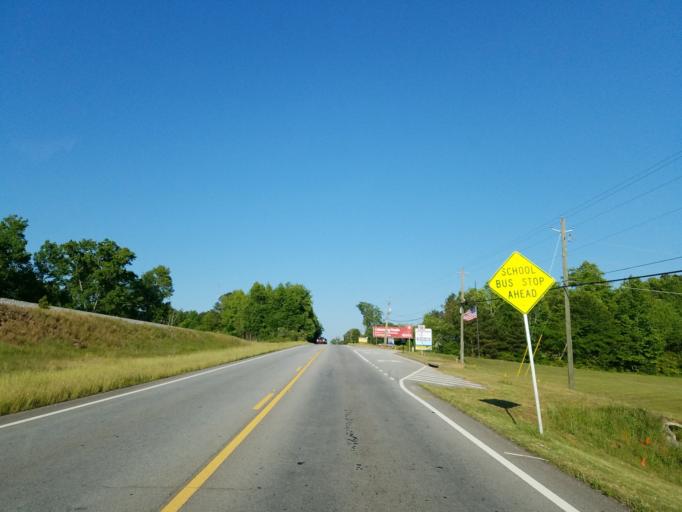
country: US
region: Georgia
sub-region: Douglas County
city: Douglasville
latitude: 33.7304
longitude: -84.8085
